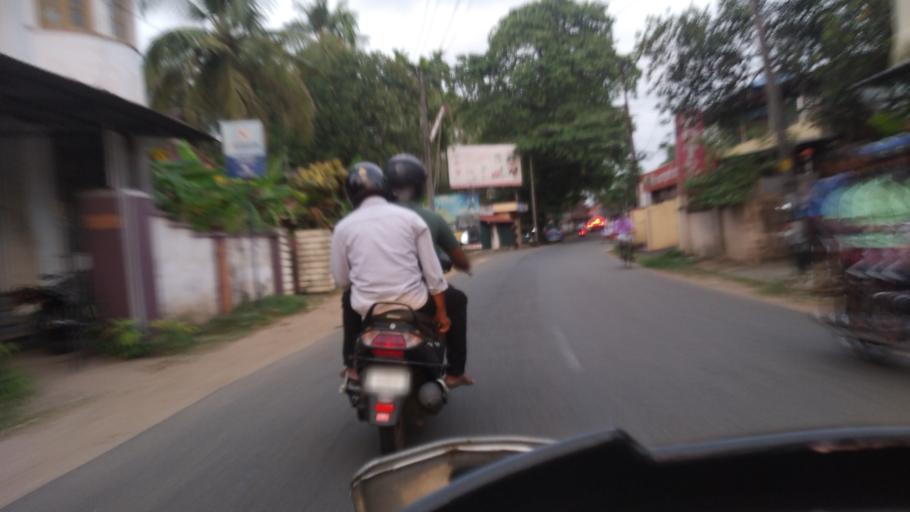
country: IN
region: Kerala
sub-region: Thrissur District
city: Kodungallur
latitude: 10.1514
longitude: 76.2223
